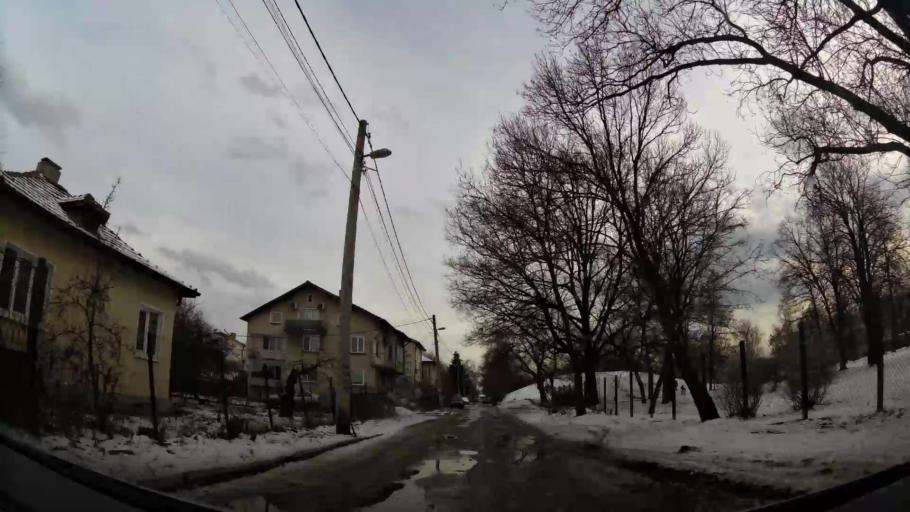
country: BG
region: Sofia-Capital
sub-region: Stolichna Obshtina
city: Sofia
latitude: 42.7265
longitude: 23.3400
